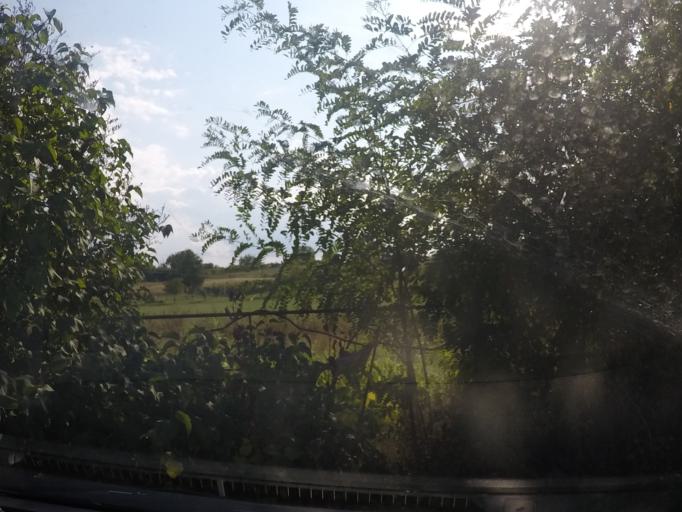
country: SK
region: Nitriansky
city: Levice
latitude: 48.2543
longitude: 18.6671
